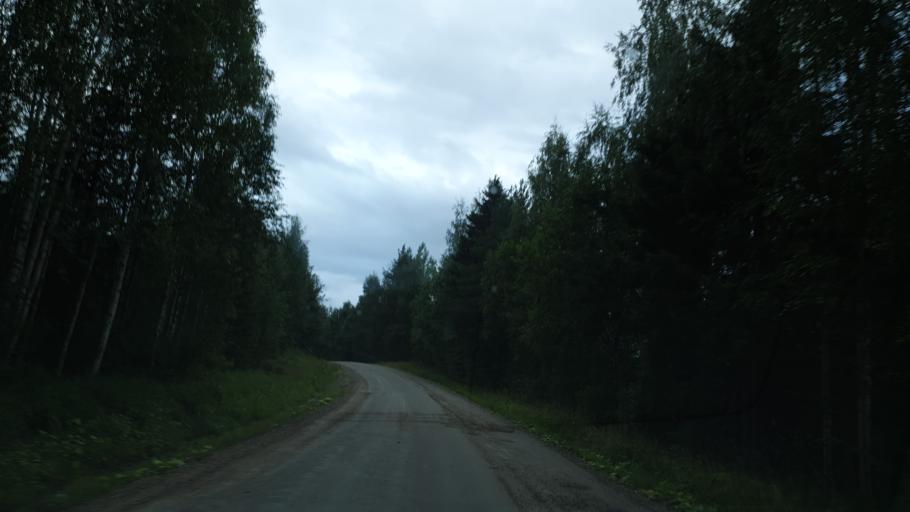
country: FI
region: Kainuu
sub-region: Kehys-Kainuu
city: Kuhmo
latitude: 64.1977
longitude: 29.3664
